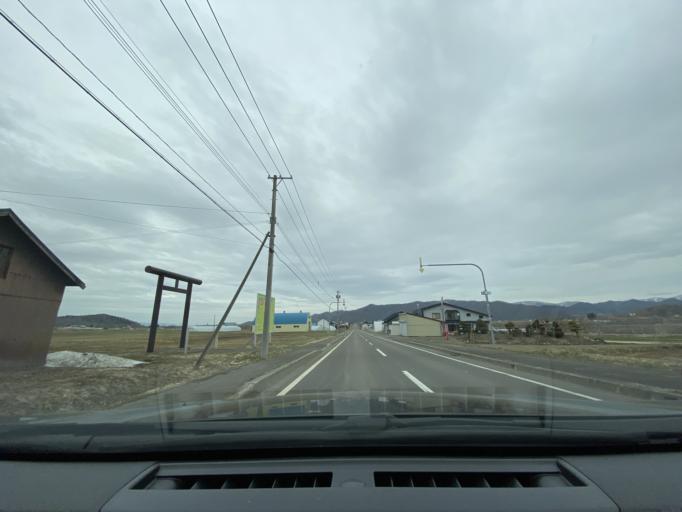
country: JP
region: Hokkaido
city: Nayoro
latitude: 44.1088
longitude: 142.4783
